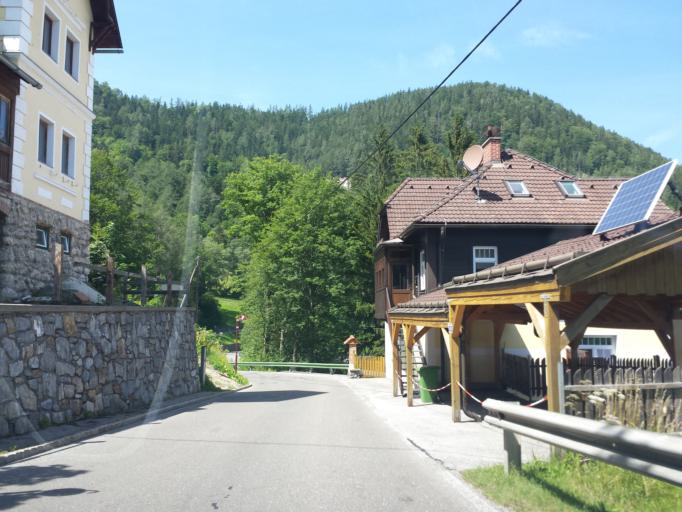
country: AT
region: Lower Austria
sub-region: Politischer Bezirk Neunkirchen
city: Semmering
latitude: 47.6372
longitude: 15.8325
